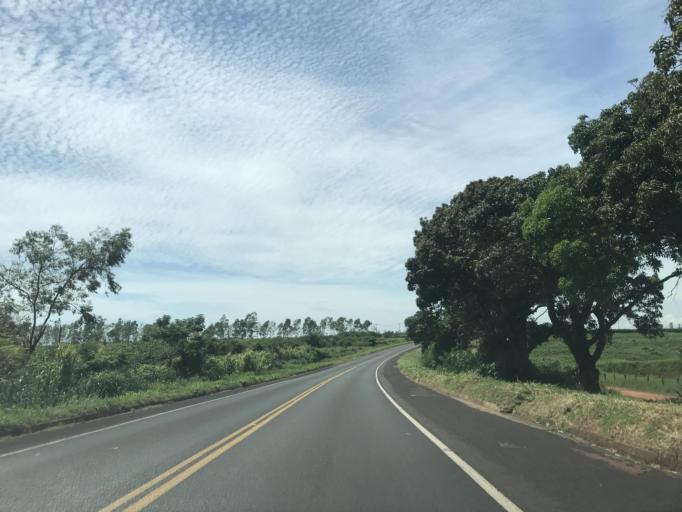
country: BR
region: Parana
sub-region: Paranavai
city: Nova Aurora
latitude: -22.9744
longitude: -52.6092
